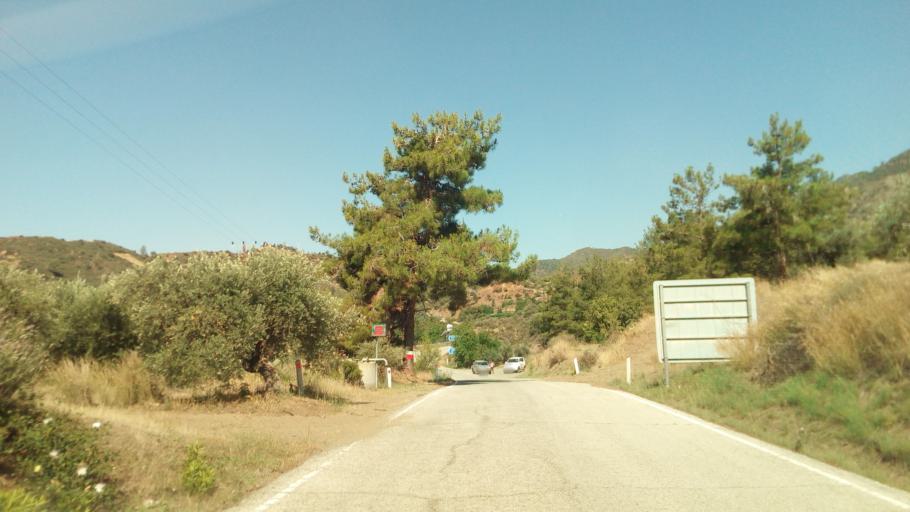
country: CY
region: Limassol
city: Parekklisha
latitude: 34.8643
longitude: 33.1695
